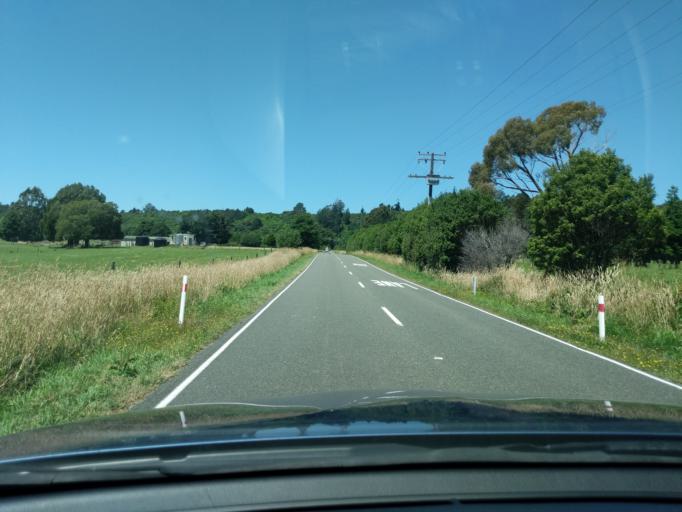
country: NZ
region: Tasman
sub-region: Tasman District
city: Takaka
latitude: -40.7291
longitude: 172.6310
